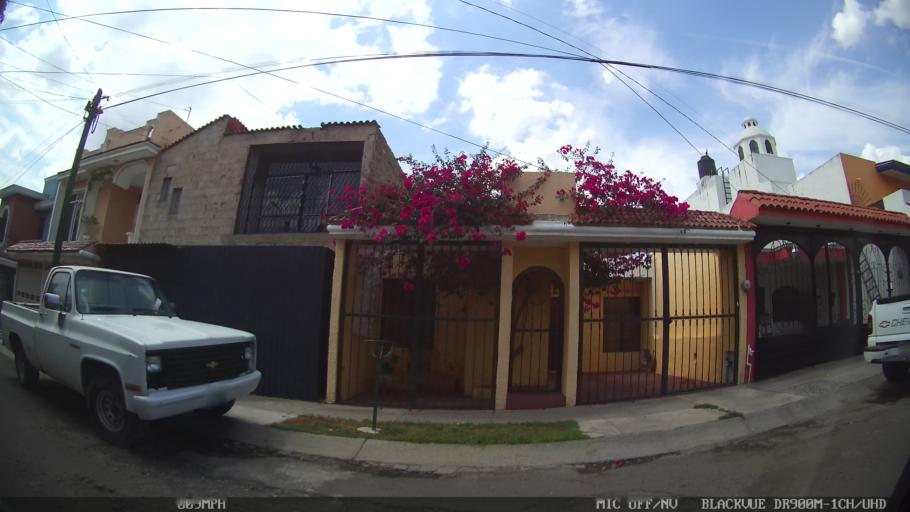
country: MX
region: Jalisco
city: Tonala
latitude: 20.6240
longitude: -103.2592
